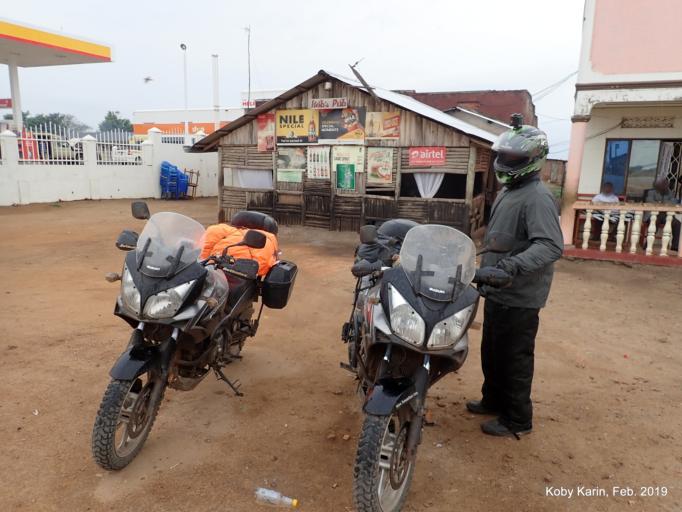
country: UG
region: Western Region
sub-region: Rubirizi District
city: Rubirizi
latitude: -0.1208
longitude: 30.0479
